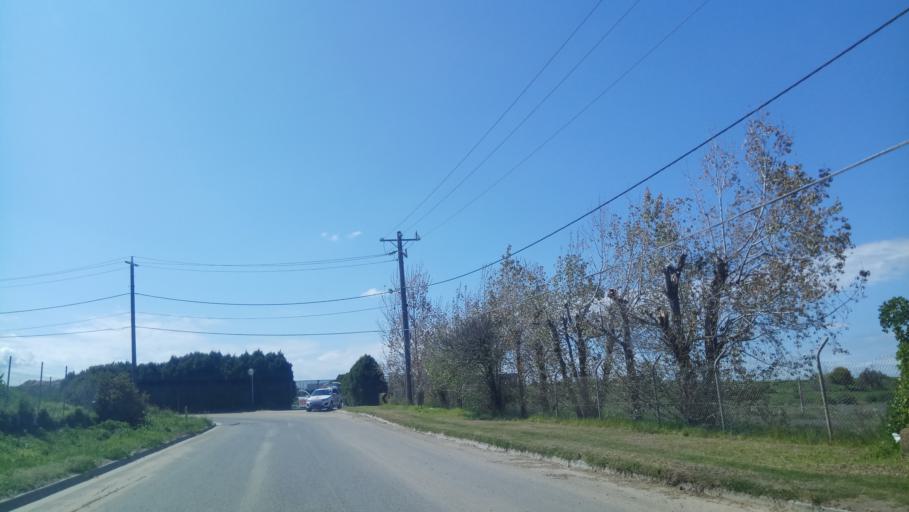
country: AU
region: Victoria
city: Heatherton
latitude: -37.9651
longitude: 145.1160
